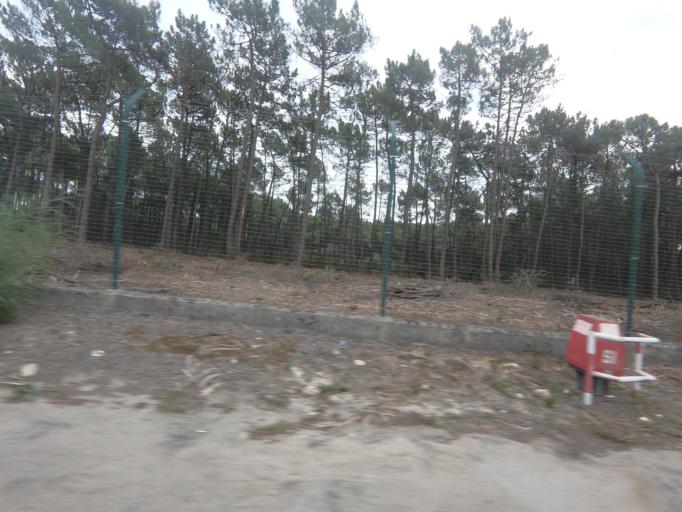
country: PT
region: Setubal
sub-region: Almada
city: Charneca
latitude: 38.5911
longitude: -9.1914
